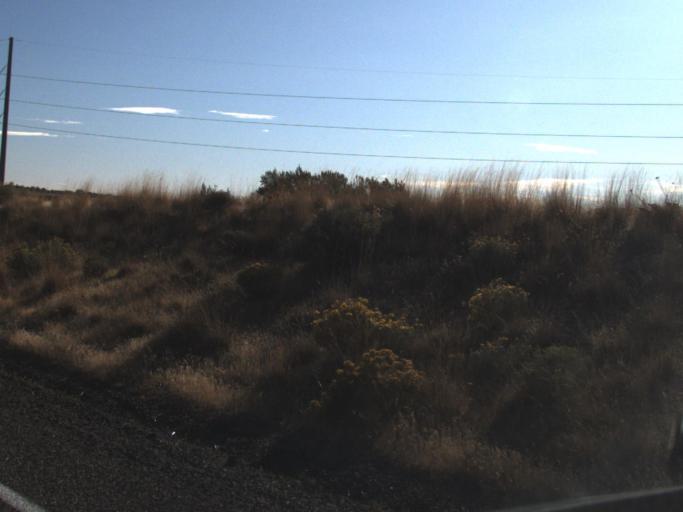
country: US
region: Washington
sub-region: Benton County
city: West Richland
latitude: 46.2772
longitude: -119.4063
